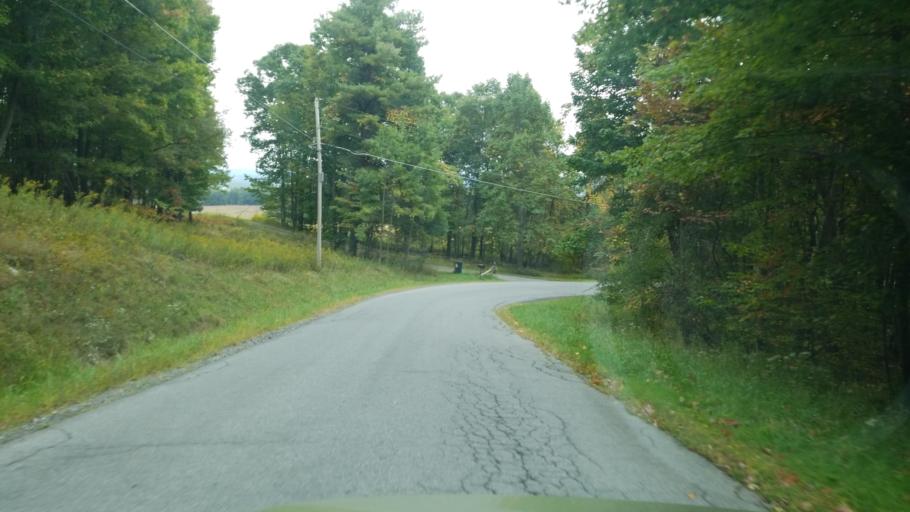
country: US
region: Pennsylvania
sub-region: Clearfield County
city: Curwensville
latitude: 41.0106
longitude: -78.5396
